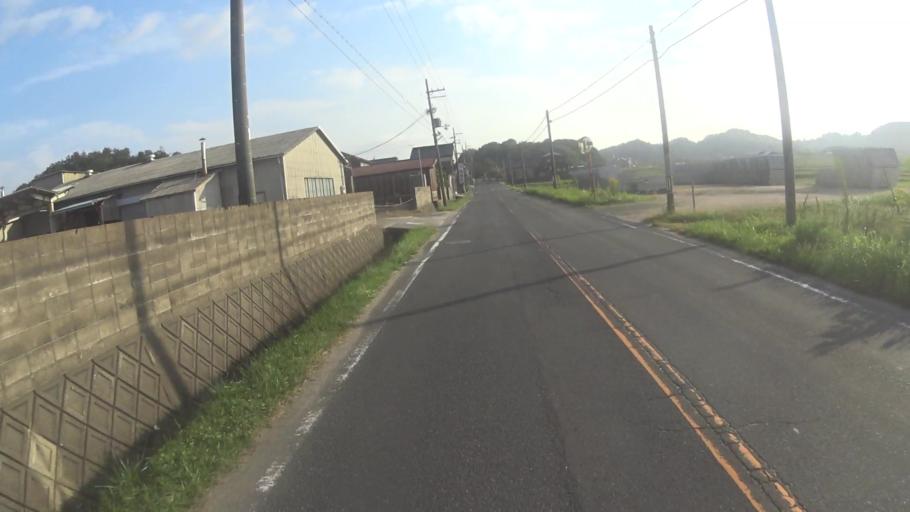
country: JP
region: Kyoto
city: Miyazu
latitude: 35.6672
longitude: 135.0915
